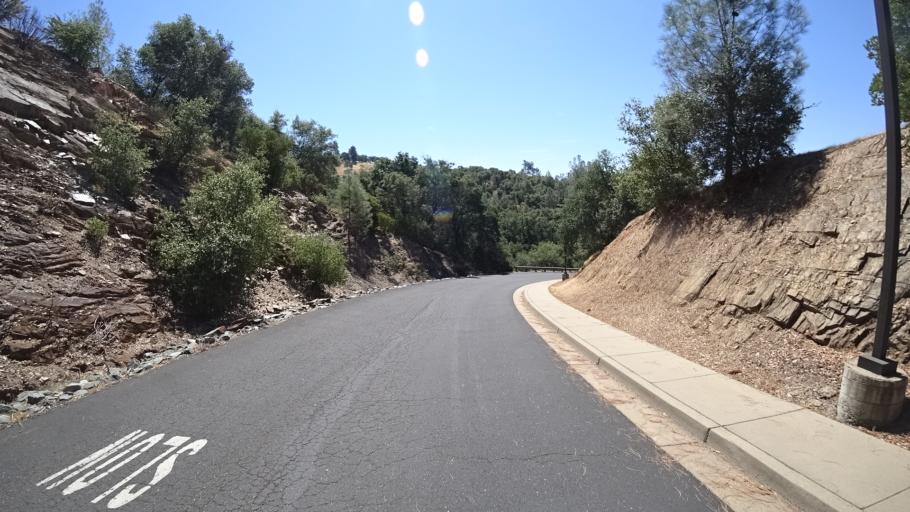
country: US
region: California
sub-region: Calaveras County
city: Angels Camp
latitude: 38.0764
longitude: -120.5353
